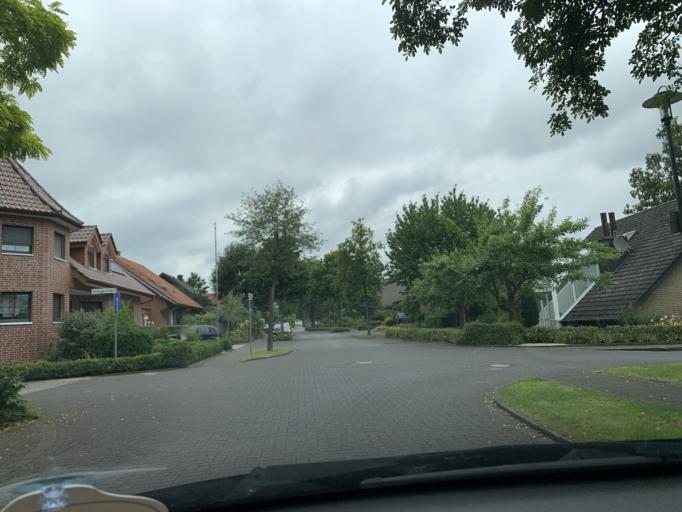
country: DE
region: North Rhine-Westphalia
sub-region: Regierungsbezirk Munster
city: Wadersloh
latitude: 51.7386
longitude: 8.2389
